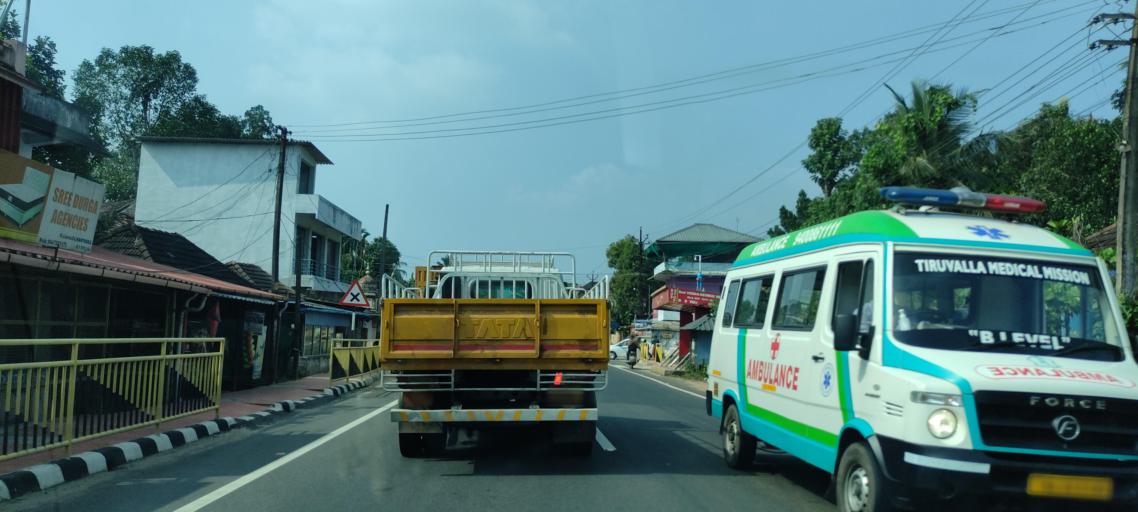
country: IN
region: Kerala
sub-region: Alappuzha
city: Chengannur
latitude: 9.2544
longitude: 76.6621
